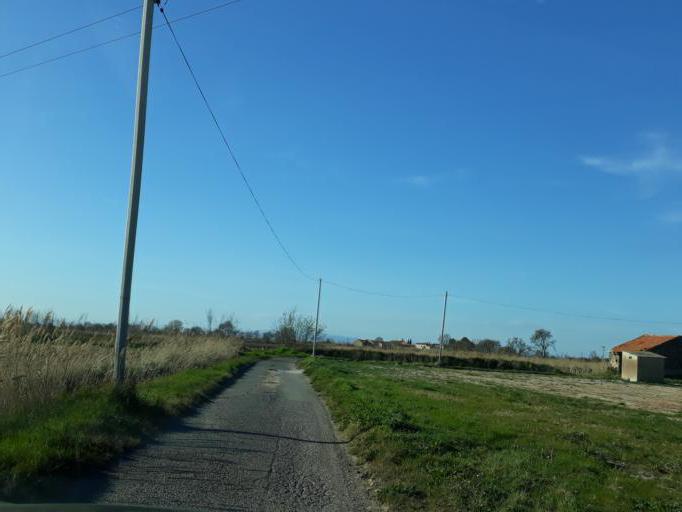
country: FR
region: Languedoc-Roussillon
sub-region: Departement de l'Herault
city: Agde
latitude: 43.3224
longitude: 3.4569
